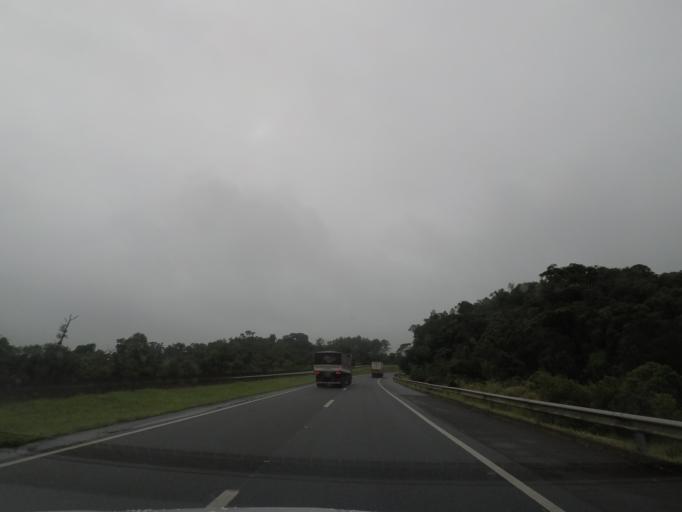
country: BR
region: Sao Paulo
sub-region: Cajati
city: Cajati
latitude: -24.9705
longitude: -48.3673
